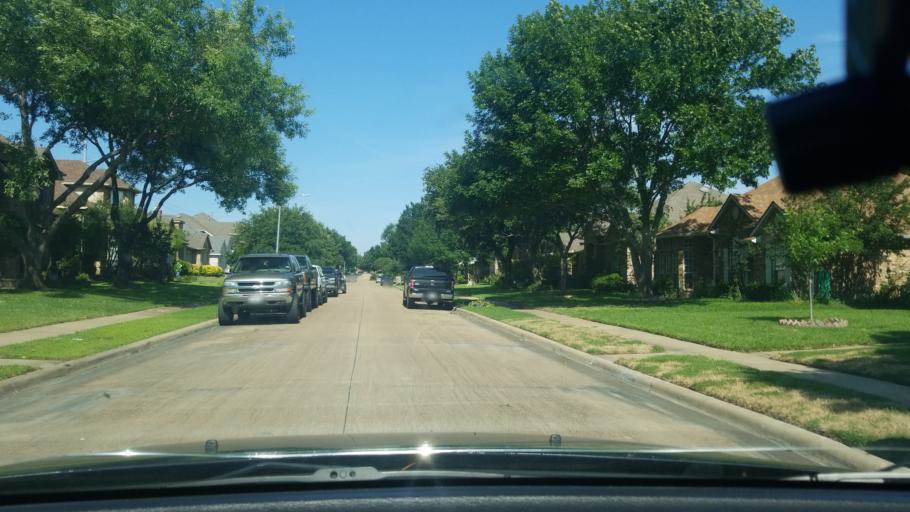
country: US
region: Texas
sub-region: Dallas County
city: Mesquite
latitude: 32.7760
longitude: -96.5871
